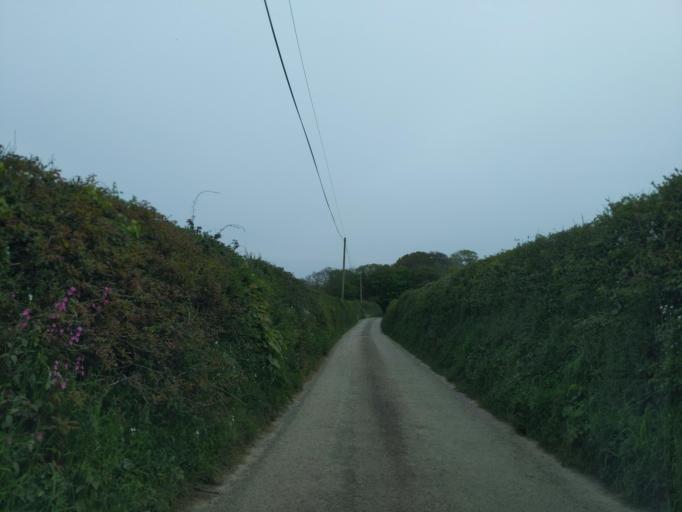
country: GB
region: England
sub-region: Cornwall
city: St Austell
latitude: 50.3094
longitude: -4.7658
